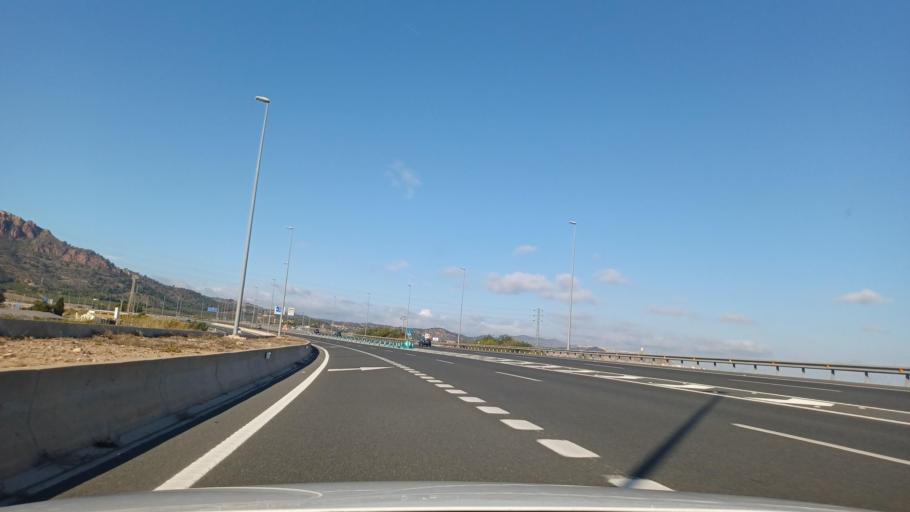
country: ES
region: Valencia
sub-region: Provincia de Valencia
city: Pucol
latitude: 39.6231
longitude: -0.2953
